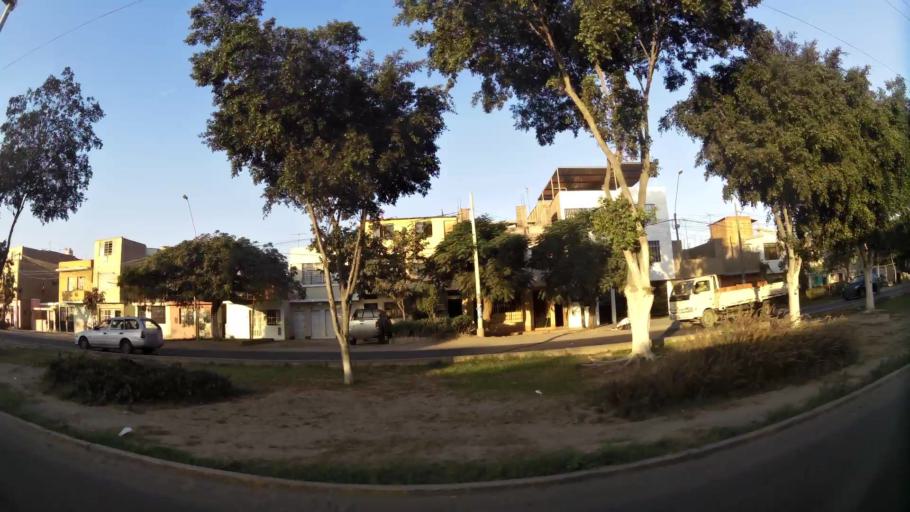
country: PE
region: Ica
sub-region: Provincia de Ica
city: Ica
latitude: -14.0733
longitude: -75.7238
